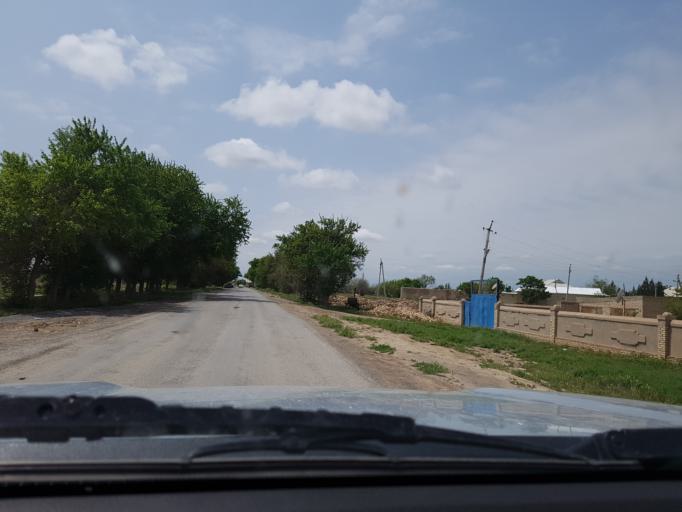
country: TM
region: Mary
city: Bayramaly
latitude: 37.6588
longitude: 62.1137
